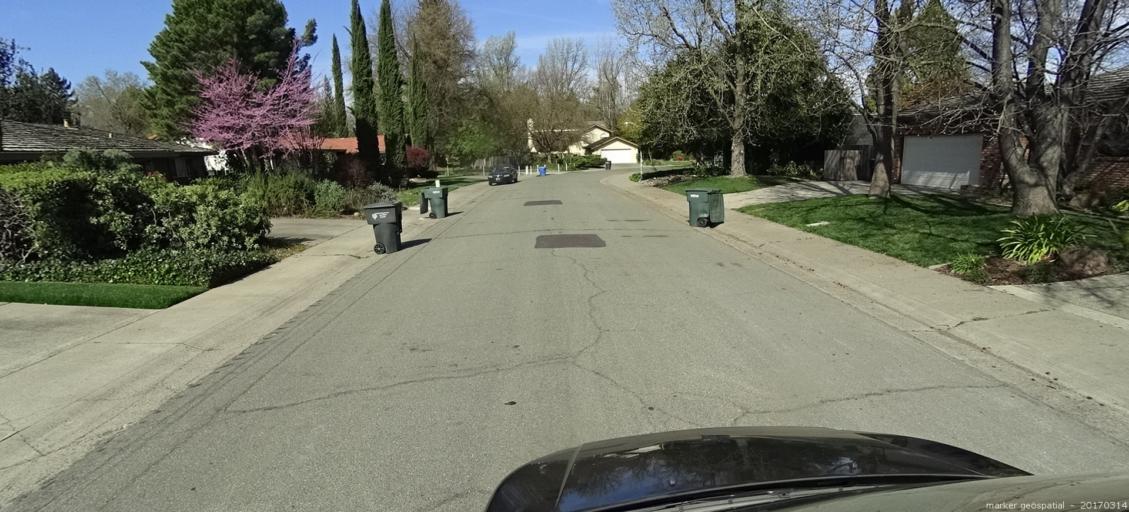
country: US
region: California
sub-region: Sacramento County
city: Parkway
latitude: 38.5041
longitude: -121.5235
